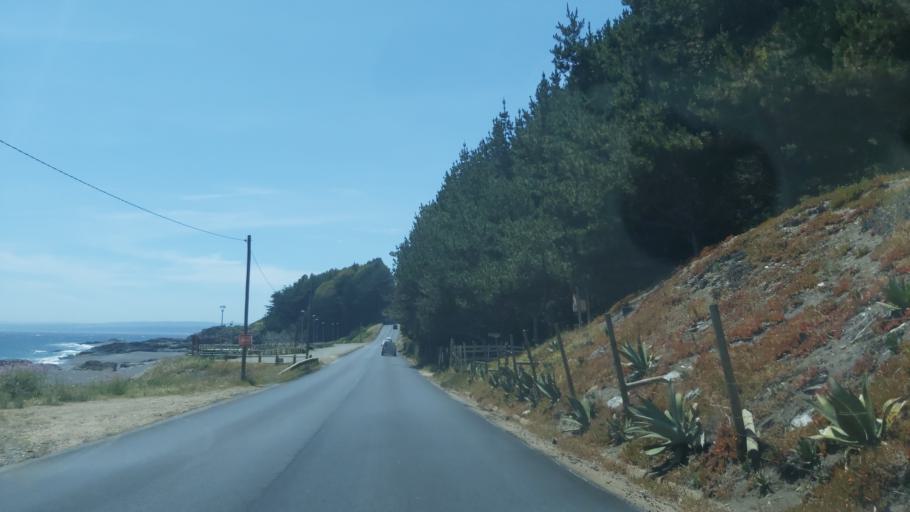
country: CL
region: Maule
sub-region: Provincia de Cauquenes
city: Cauquenes
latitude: -35.8303
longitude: -72.6184
